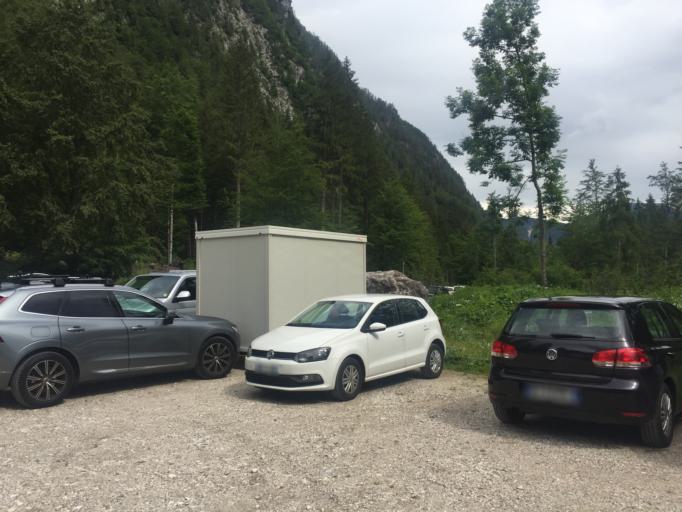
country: IT
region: Friuli Venezia Giulia
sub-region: Provincia di Udine
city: Malborghetto
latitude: 46.4683
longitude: 13.4922
